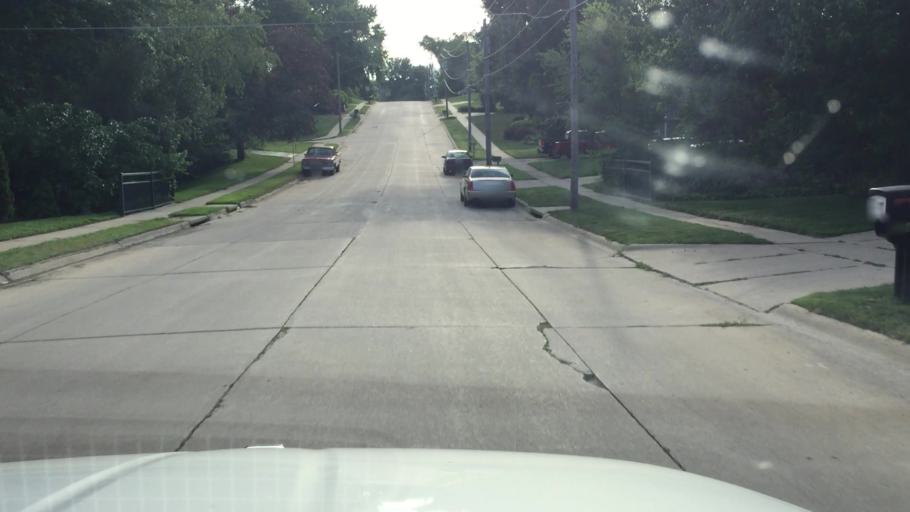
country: US
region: Iowa
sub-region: Johnson County
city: Iowa City
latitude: 41.6605
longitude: -91.4988
